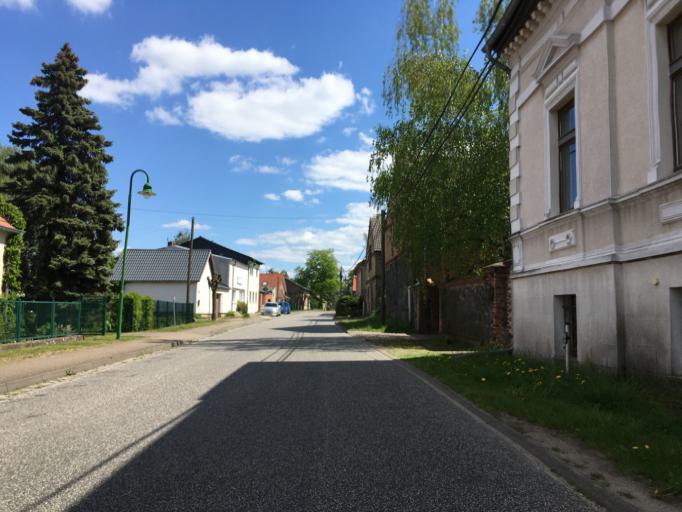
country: DE
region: Brandenburg
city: Biesenthal
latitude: 52.7351
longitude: 13.6639
